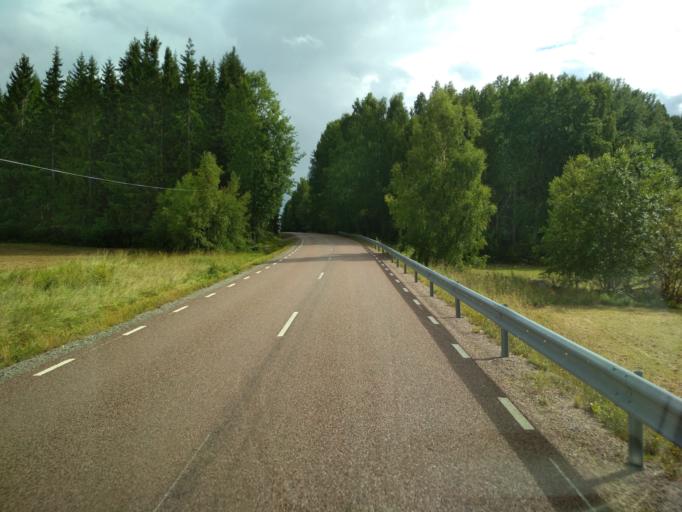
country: SE
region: Vaestmanland
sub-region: Surahammars Kommun
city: Ramnas
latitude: 59.8646
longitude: 16.0870
